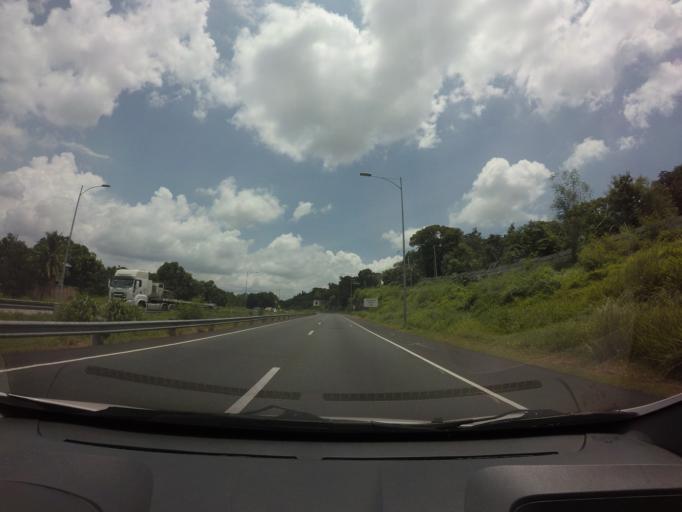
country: PH
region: Calabarzon
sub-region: Province of Laguna
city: San Pedro
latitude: 14.3813
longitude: 121.0342
